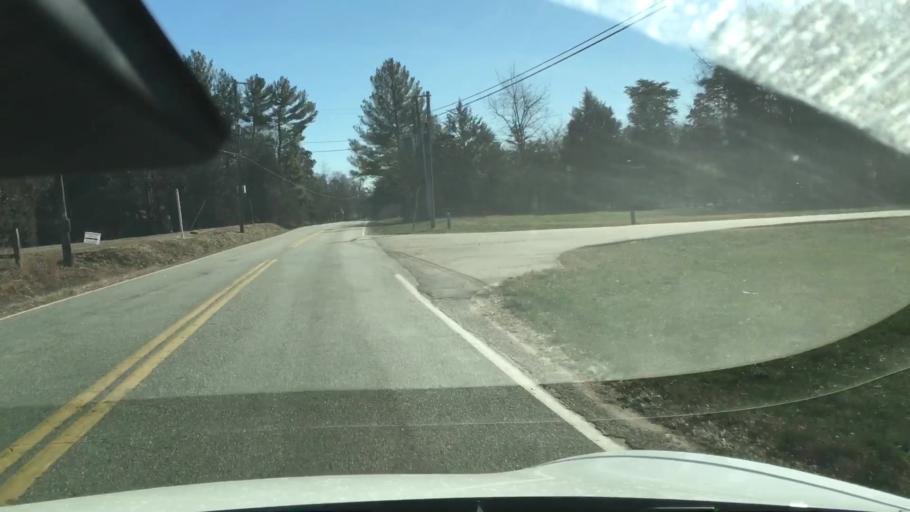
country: US
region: Virginia
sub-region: Goochland County
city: Goochland
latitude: 37.5912
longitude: -77.7583
